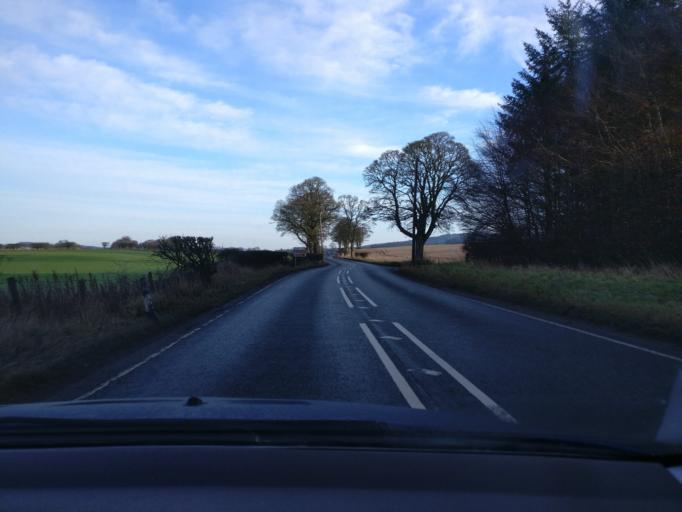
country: GB
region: Scotland
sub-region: The Scottish Borders
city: Saint Boswells
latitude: 55.4645
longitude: -2.6678
